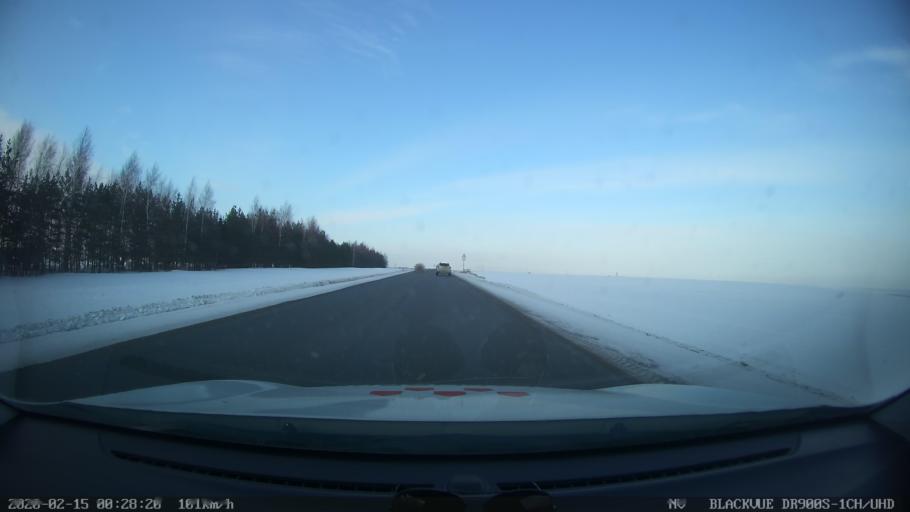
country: RU
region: Tatarstan
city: Verkhniy Uslon
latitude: 55.6405
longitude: 48.8756
